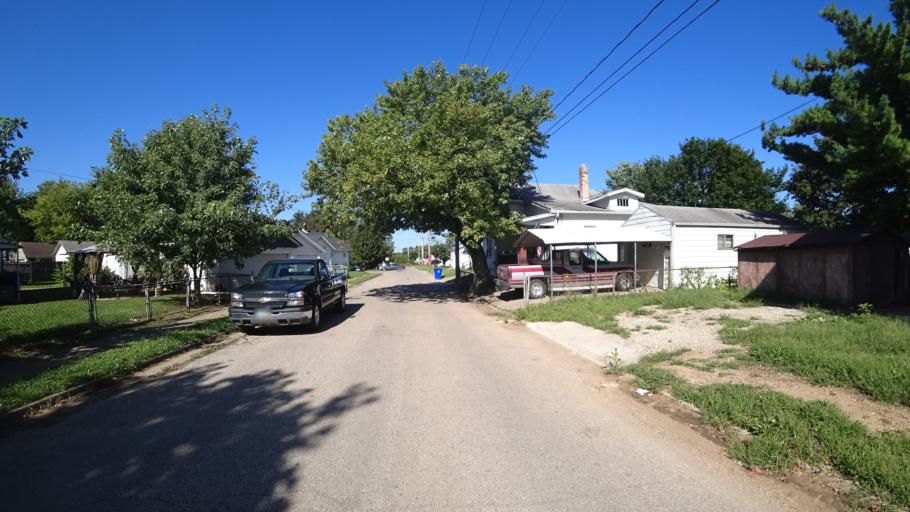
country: US
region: Ohio
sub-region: Butler County
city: Hamilton
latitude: 39.3987
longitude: -84.5424
